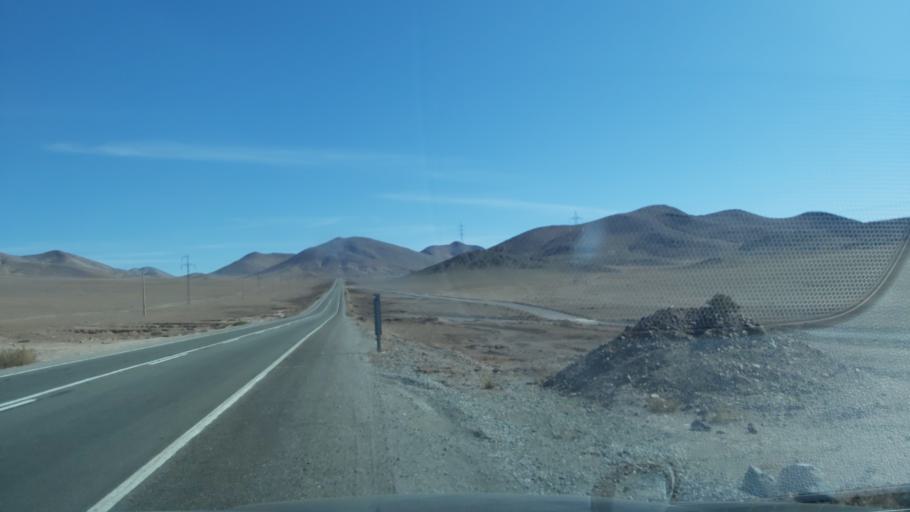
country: CL
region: Atacama
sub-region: Provincia de Copiapo
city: Copiapo
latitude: -27.1079
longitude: -69.9606
